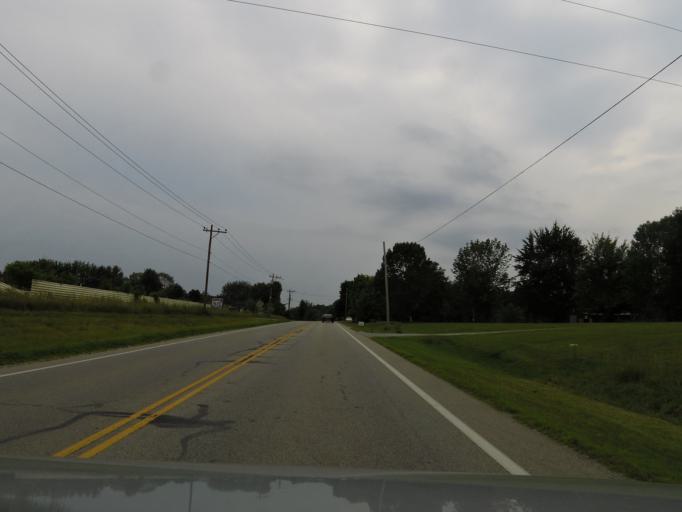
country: US
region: Ohio
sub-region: Brown County
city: Georgetown
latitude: 38.9393
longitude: -83.9033
